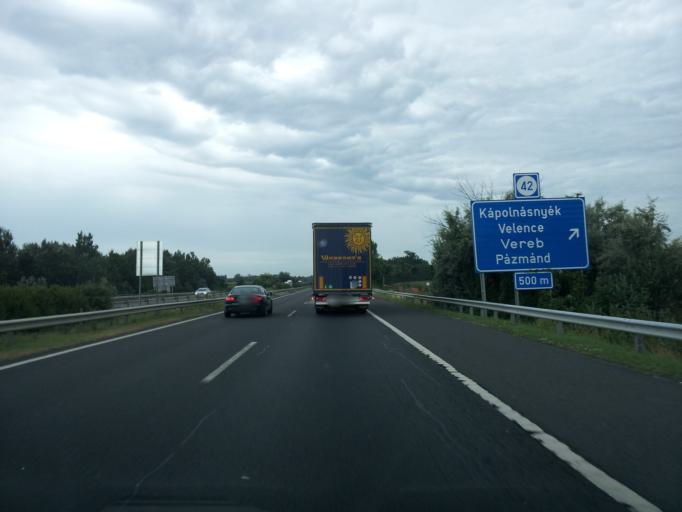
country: HU
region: Fejer
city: Kapolnasnyek
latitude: 47.2645
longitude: 18.6845
